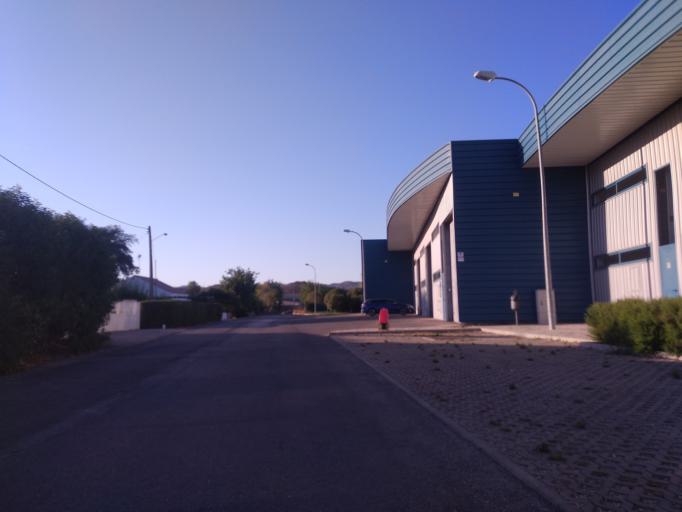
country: PT
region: Faro
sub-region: Sao Bras de Alportel
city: Sao Bras de Alportel
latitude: 37.1680
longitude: -7.8931
